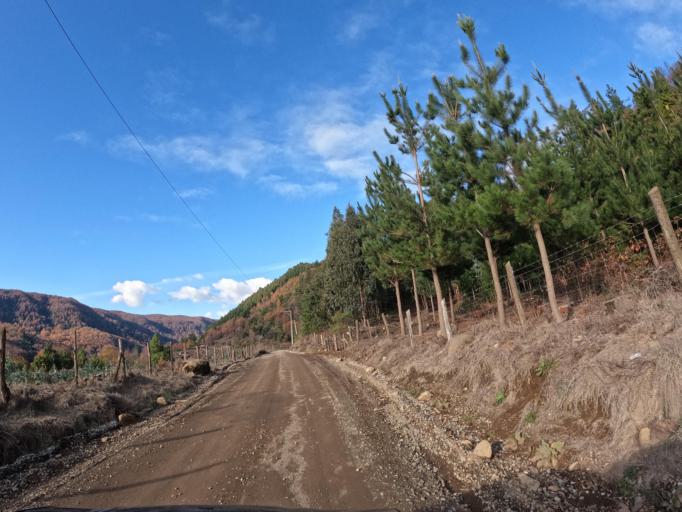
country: CL
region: Biobio
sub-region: Provincia de Nuble
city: Coihueco
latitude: -36.8005
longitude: -71.6911
